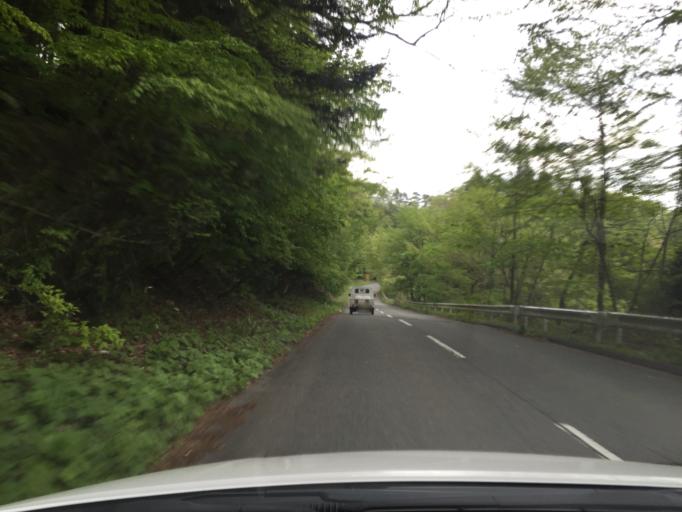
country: JP
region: Miyagi
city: Marumori
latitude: 37.7235
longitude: 140.8017
